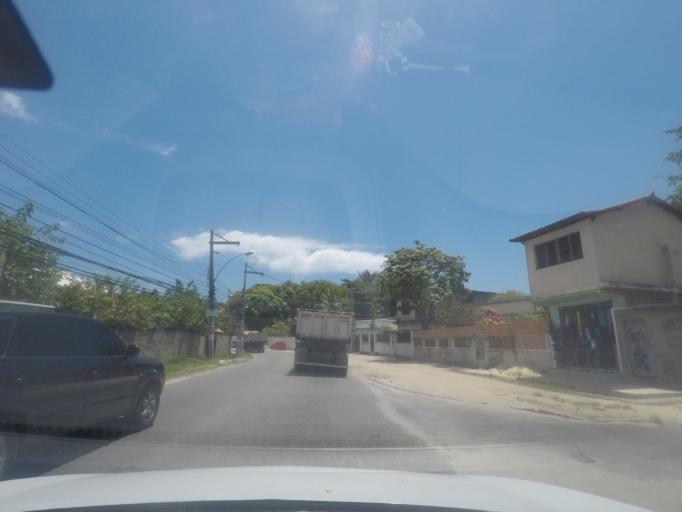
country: BR
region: Rio de Janeiro
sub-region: Itaguai
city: Itaguai
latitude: -22.9317
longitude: -43.6901
